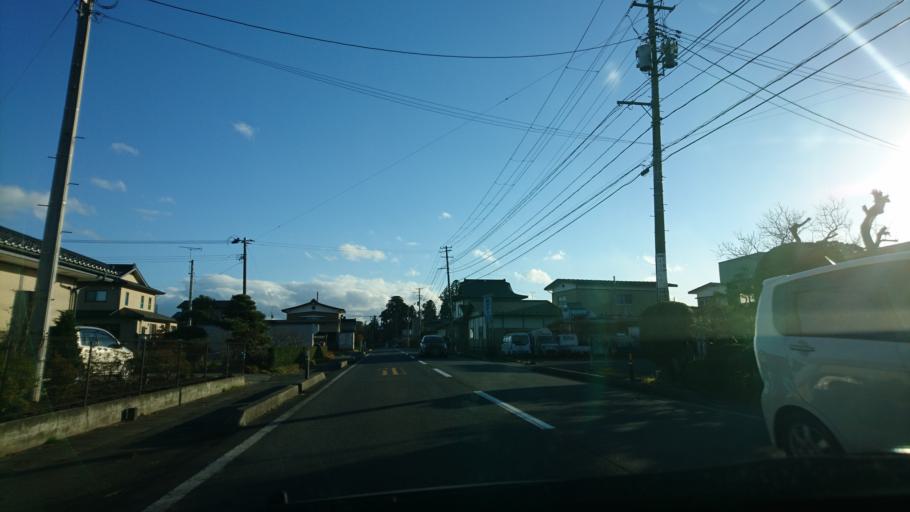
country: JP
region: Iwate
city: Ichinoseki
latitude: 38.9796
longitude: 141.1164
